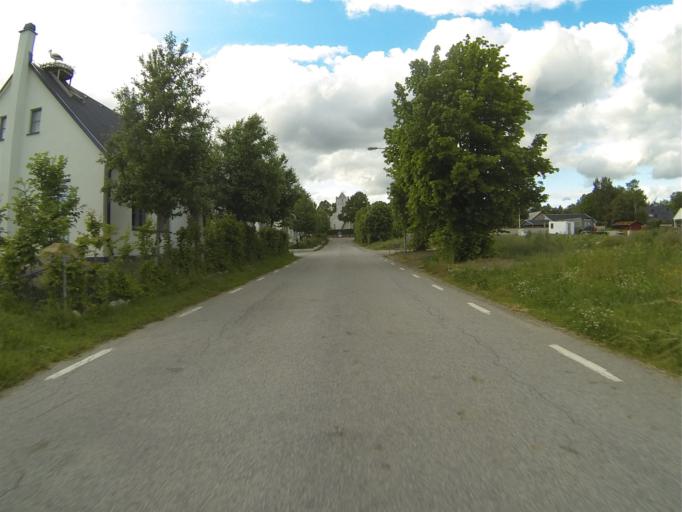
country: SE
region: Skane
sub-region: Lunds Kommun
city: Lund
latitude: 55.6847
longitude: 13.2251
